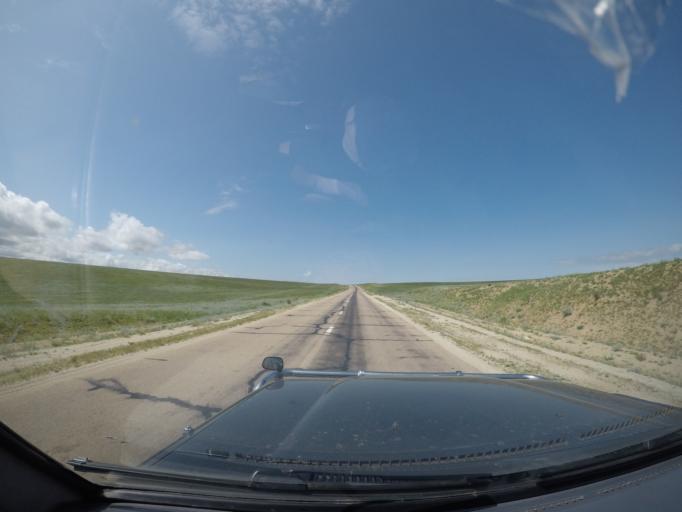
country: MN
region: Hentiy
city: Bayan
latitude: 47.2943
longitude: 111.1729
